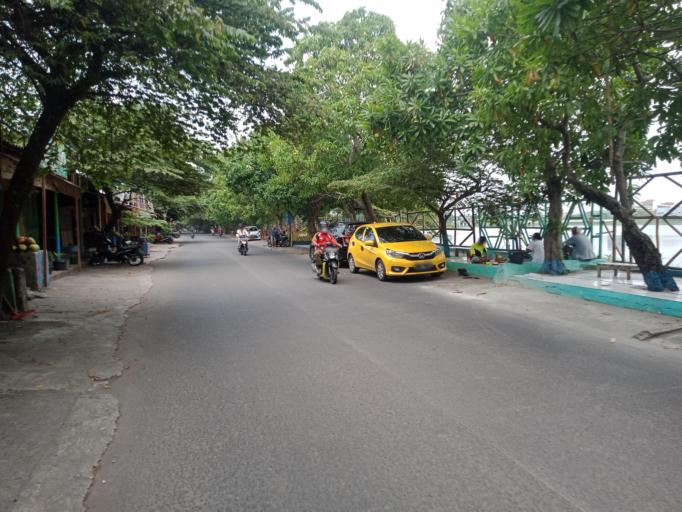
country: ID
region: Banten
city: Tangerang
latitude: -6.1617
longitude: 106.5900
